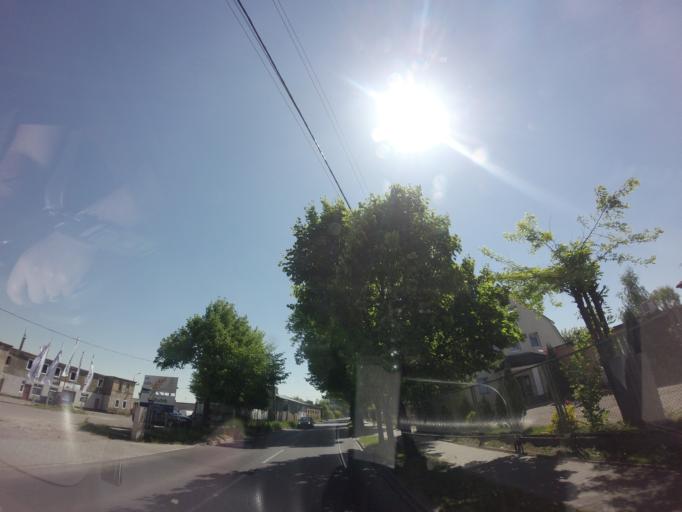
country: PL
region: West Pomeranian Voivodeship
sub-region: Powiat pyrzycki
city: Lipiany
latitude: 53.0035
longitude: 14.9763
